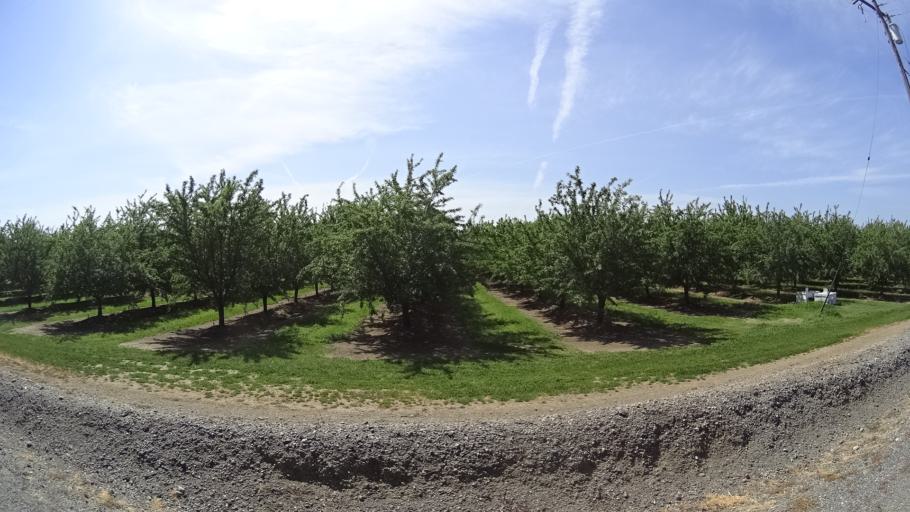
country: US
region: California
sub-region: Glenn County
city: Hamilton City
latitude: 39.8042
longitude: -122.0945
